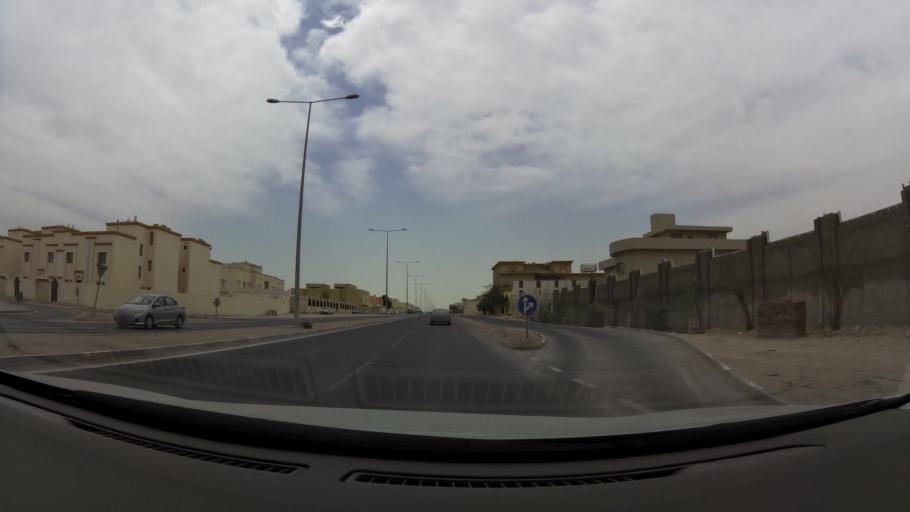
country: QA
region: Baladiyat ad Dawhah
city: Doha
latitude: 25.2288
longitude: 51.4702
